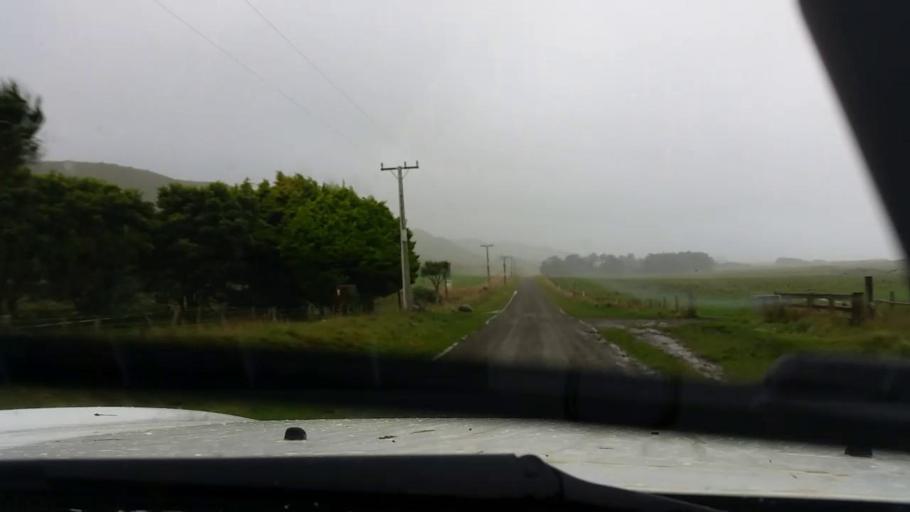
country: NZ
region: Wellington
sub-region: Masterton District
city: Masterton
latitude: -41.2571
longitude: 175.9043
